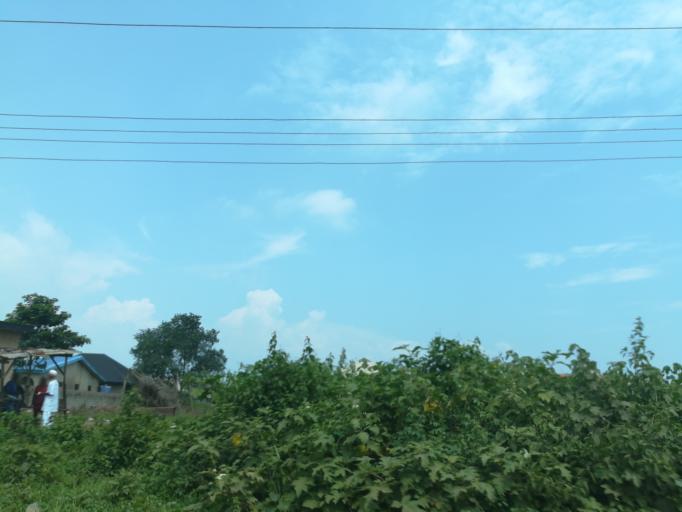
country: NG
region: Lagos
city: Ikorodu
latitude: 6.5944
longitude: 3.6247
